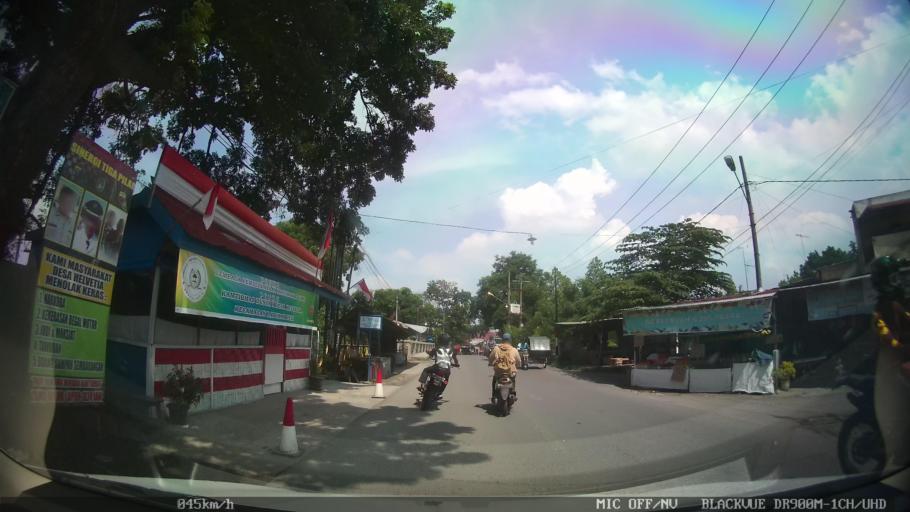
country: ID
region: North Sumatra
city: Medan
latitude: 3.6243
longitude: 98.6639
